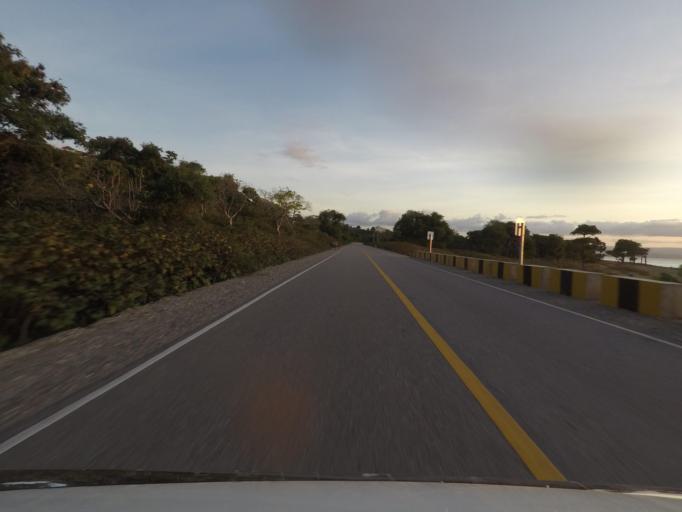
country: TL
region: Baucau
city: Baucau
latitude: -8.4594
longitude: 126.6117
